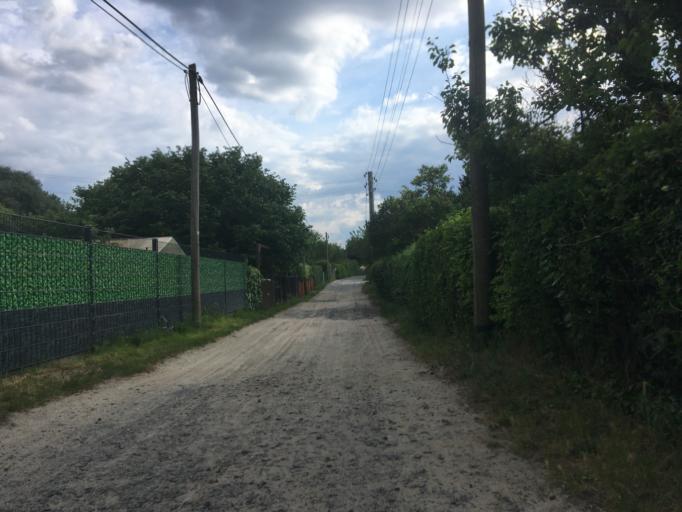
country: DE
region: Berlin
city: Johannisthal
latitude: 52.4439
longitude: 13.4892
